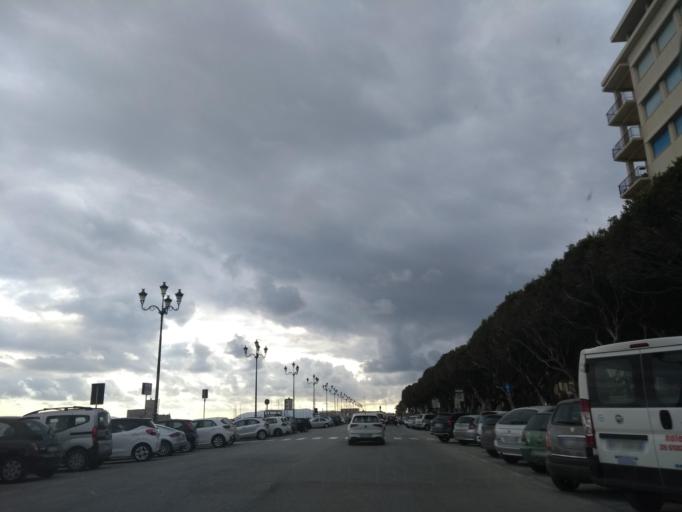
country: IT
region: Sicily
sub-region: Trapani
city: Trapani
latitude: 38.0145
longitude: 12.5057
